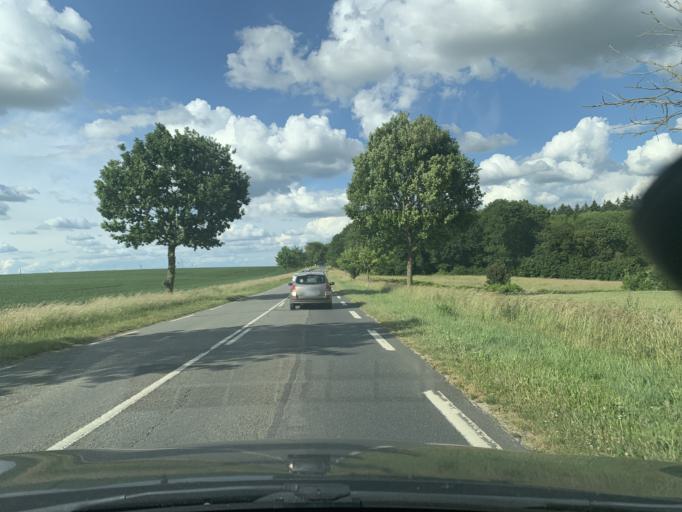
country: FR
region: Picardie
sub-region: Departement de la Somme
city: Moislains
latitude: 49.9721
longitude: 2.9907
